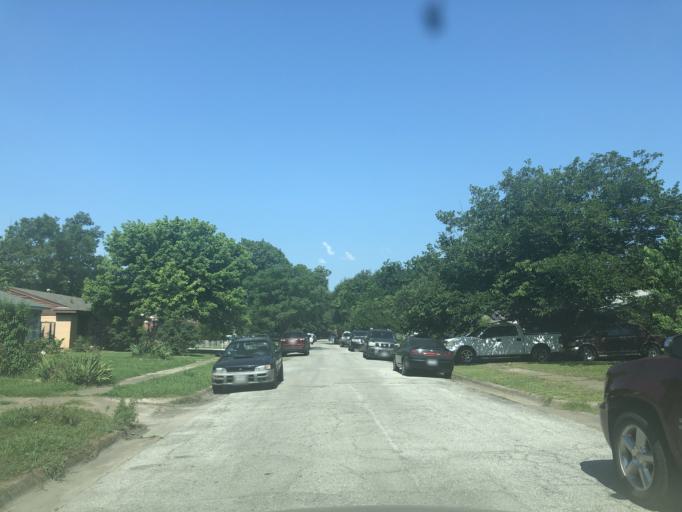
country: US
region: Texas
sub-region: Dallas County
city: Grand Prairie
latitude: 32.7174
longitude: -96.9994
